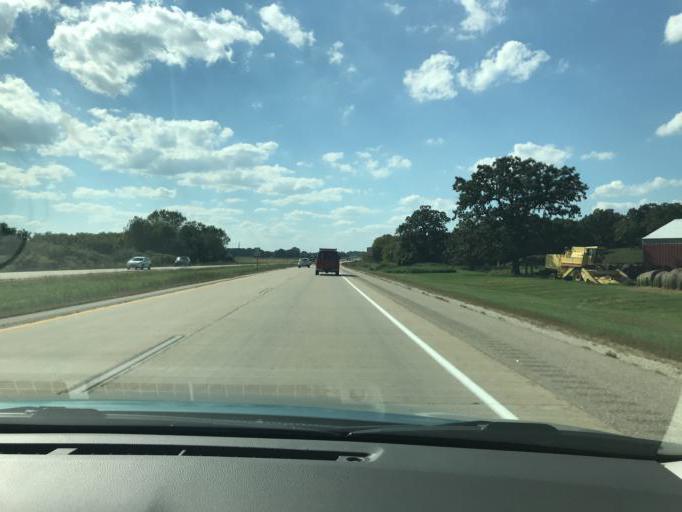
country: US
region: Wisconsin
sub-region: Kenosha County
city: Twin Lakes
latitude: 42.5820
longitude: -88.2292
